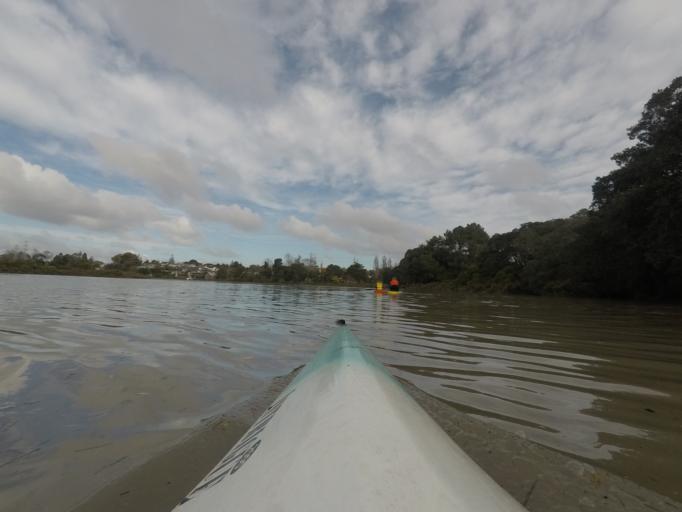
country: NZ
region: Auckland
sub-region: Auckland
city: Rosebank
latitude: -36.8967
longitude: 174.6725
